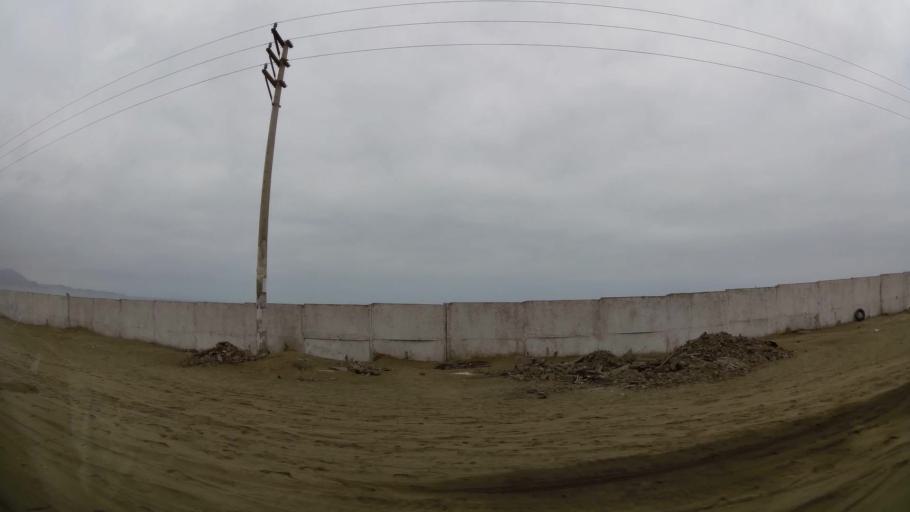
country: PE
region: Lima
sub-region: Lima
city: Punta Hermosa
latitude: -12.3527
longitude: -76.8083
